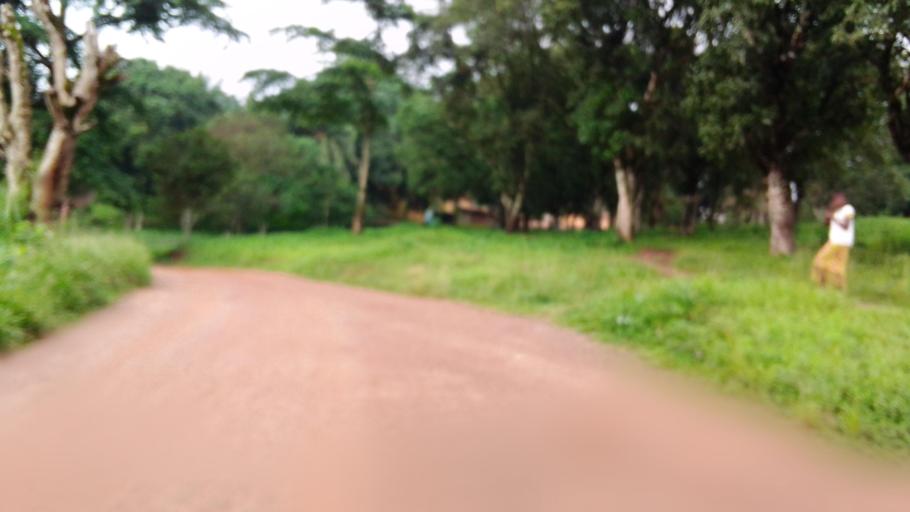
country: SL
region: Eastern Province
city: Kenema
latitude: 7.8776
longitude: -11.1756
